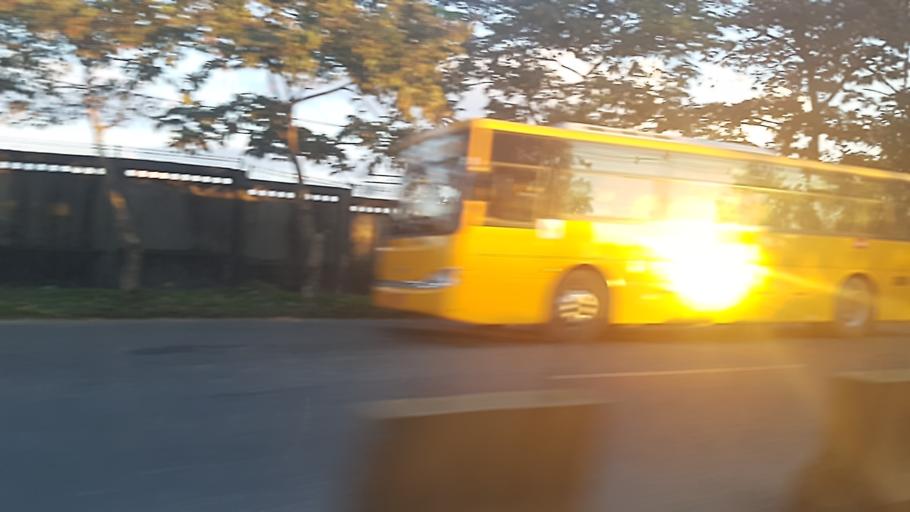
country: MM
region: Yangon
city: Yangon
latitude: 16.9083
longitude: 96.1298
